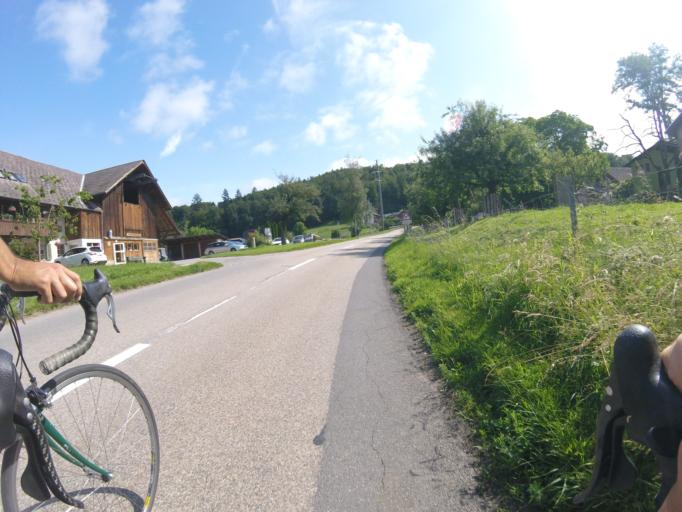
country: CH
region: Bern
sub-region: Bern-Mittelland District
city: Worb
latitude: 46.9328
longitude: 7.5721
